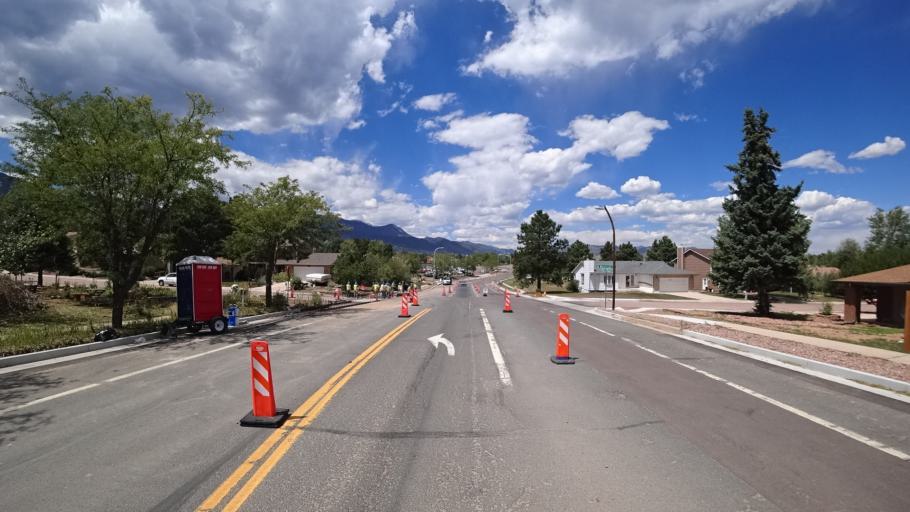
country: US
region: Colorado
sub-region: El Paso County
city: Stratmoor
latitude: 38.7876
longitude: -104.8185
